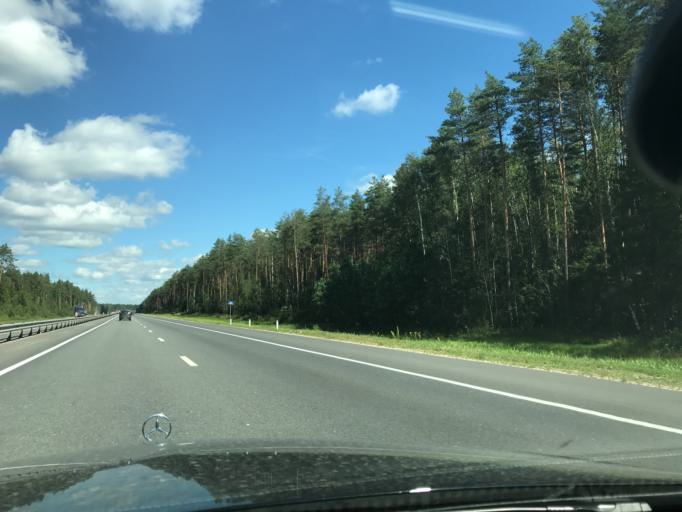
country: RU
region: Vladimir
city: Kameshkovo
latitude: 56.1791
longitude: 40.9467
